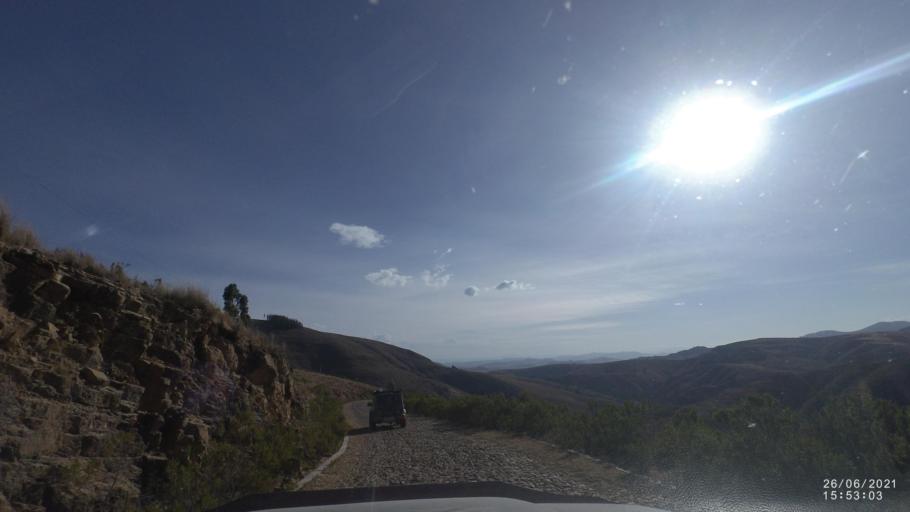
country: BO
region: Cochabamba
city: Arani
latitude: -17.8371
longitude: -65.7053
